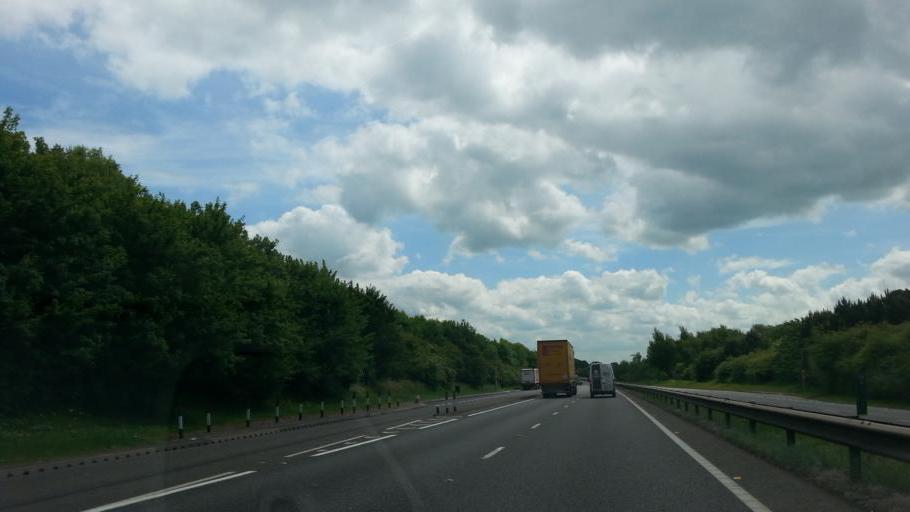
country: GB
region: England
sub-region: Derbyshire
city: Findern
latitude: 52.8670
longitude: -1.4961
